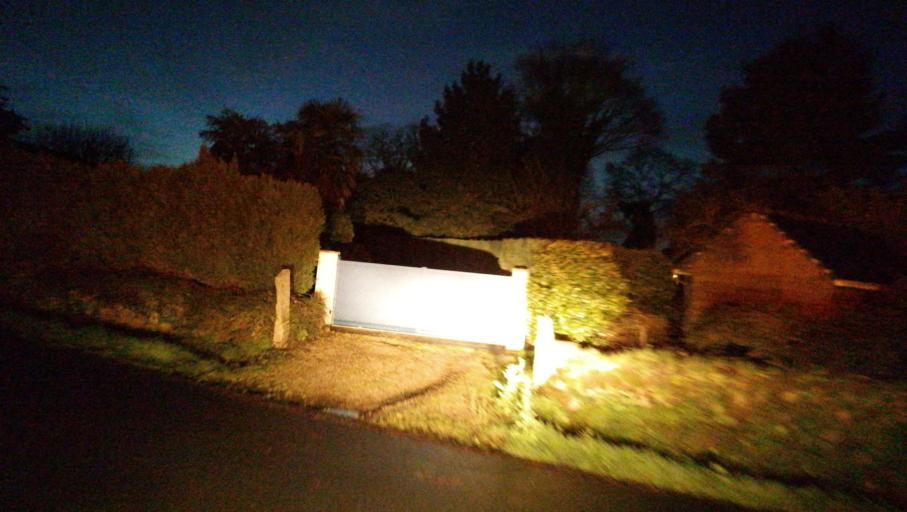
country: FR
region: Brittany
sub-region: Departement des Cotes-d'Armor
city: Plouha
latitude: 48.6751
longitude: -2.9463
